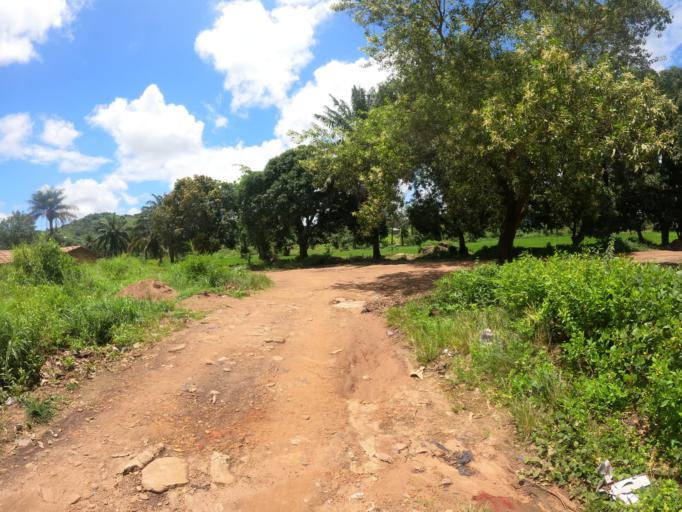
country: SL
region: Northern Province
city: Makeni
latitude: 8.8908
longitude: -12.0699
